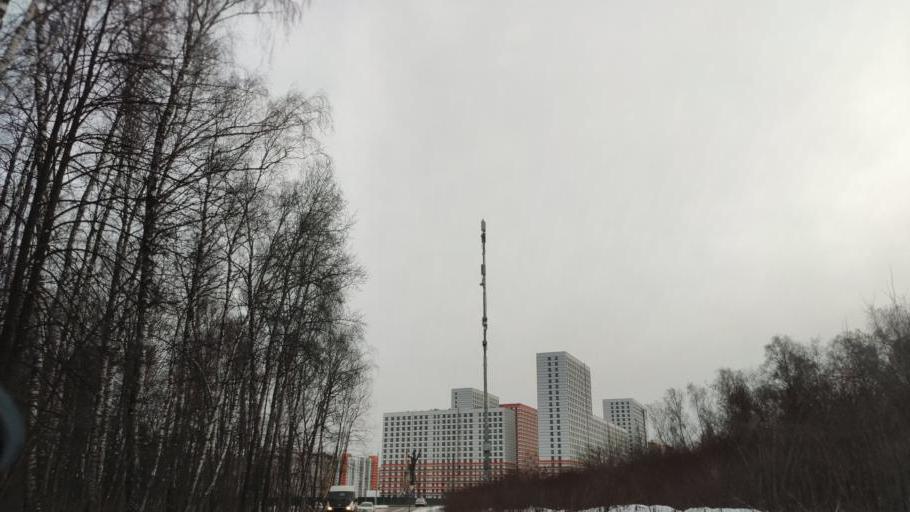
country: RU
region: Moscow
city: Annino
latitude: 55.5402
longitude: 37.6129
